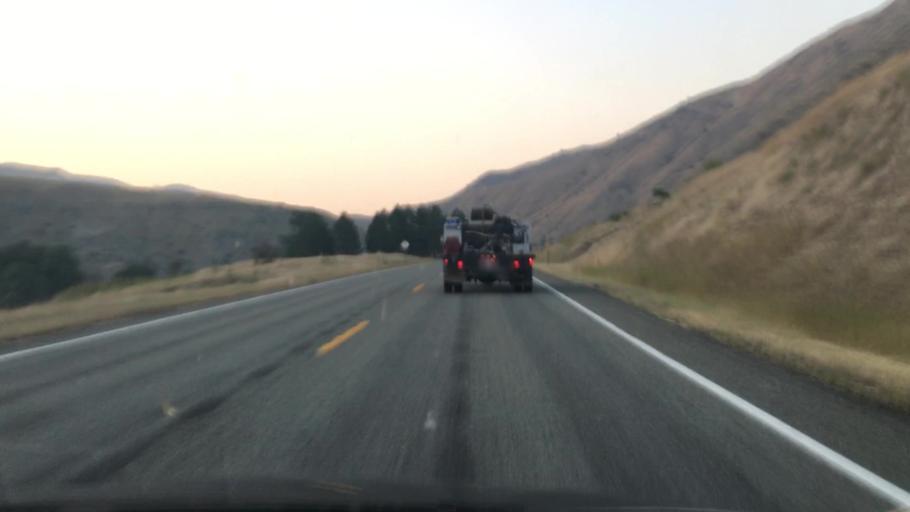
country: US
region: Idaho
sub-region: Idaho County
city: Grangeville
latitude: 45.5488
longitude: -116.3037
